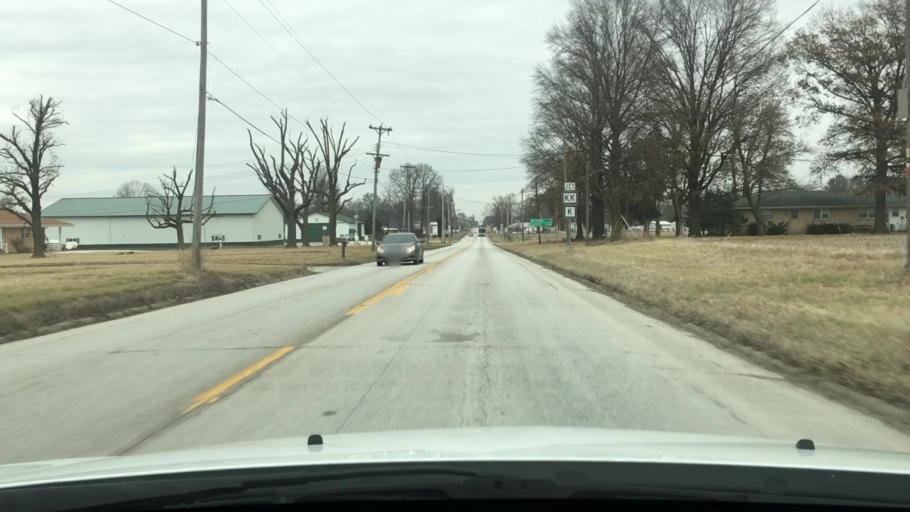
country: US
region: Missouri
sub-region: Audrain County
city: Vandalia
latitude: 39.2350
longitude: -91.6458
